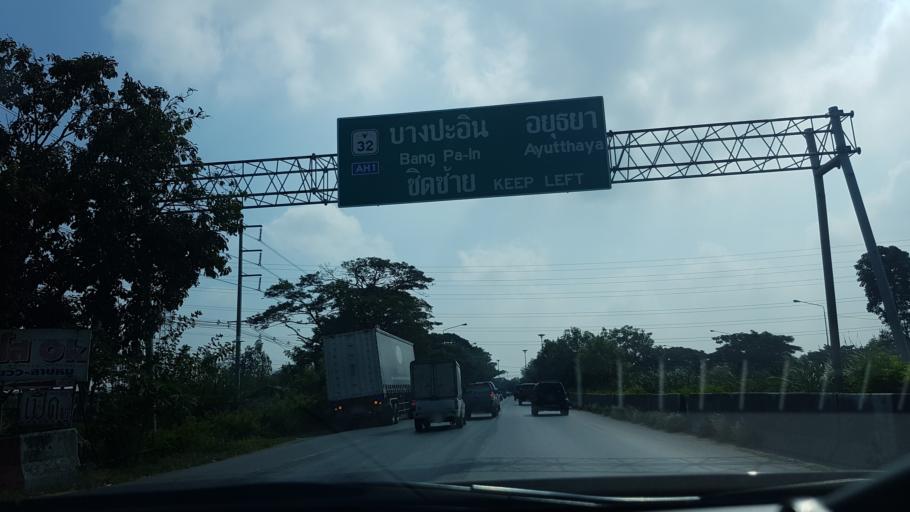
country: TH
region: Phra Nakhon Si Ayutthaya
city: Bang Pa-in
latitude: 14.1699
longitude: 100.6105
